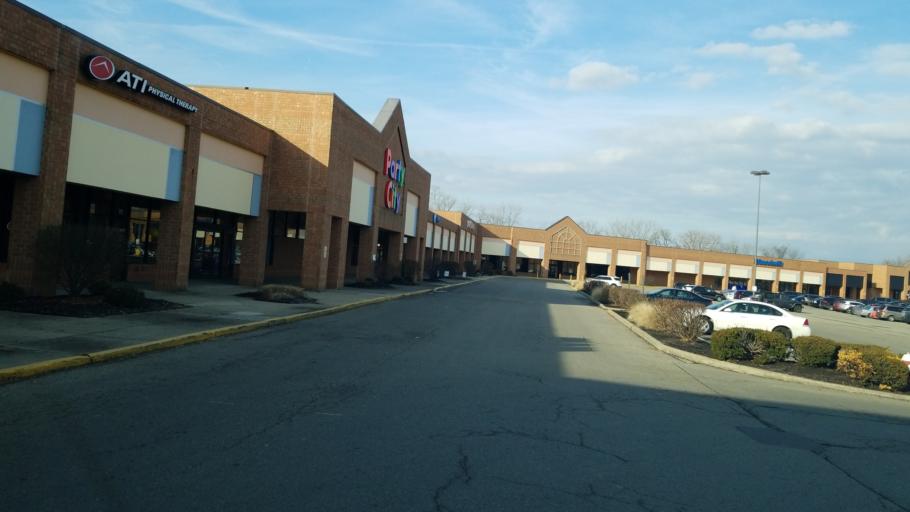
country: US
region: Ohio
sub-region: Ross County
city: Chillicothe
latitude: 39.3460
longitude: -82.9792
